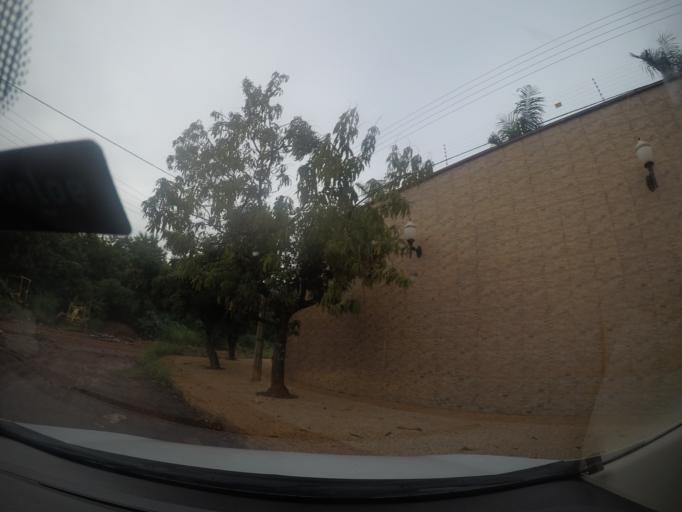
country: BR
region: Goias
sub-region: Goiania
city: Goiania
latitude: -16.6332
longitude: -49.2408
